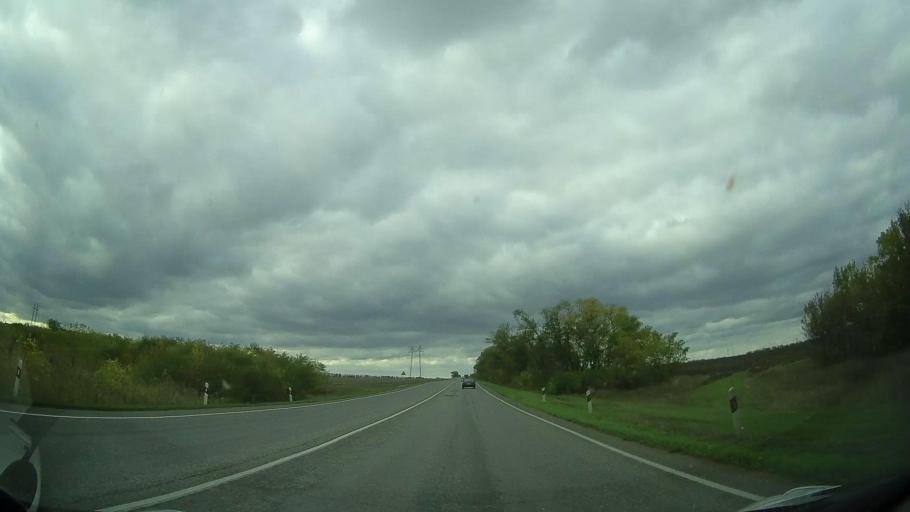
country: RU
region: Rostov
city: Zernograd
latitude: 46.8219
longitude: 40.2554
